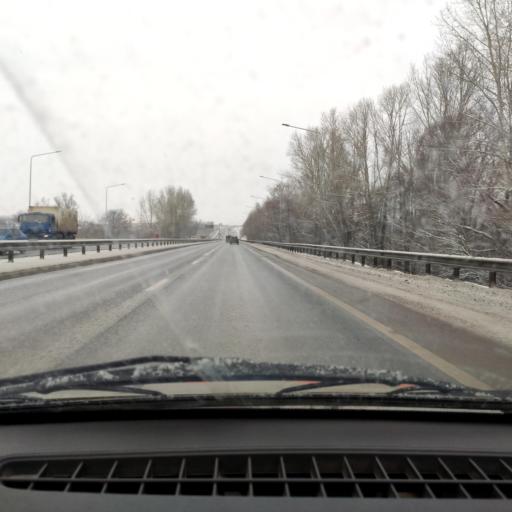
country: RU
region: Bashkortostan
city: Avdon
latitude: 54.5094
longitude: 55.9006
